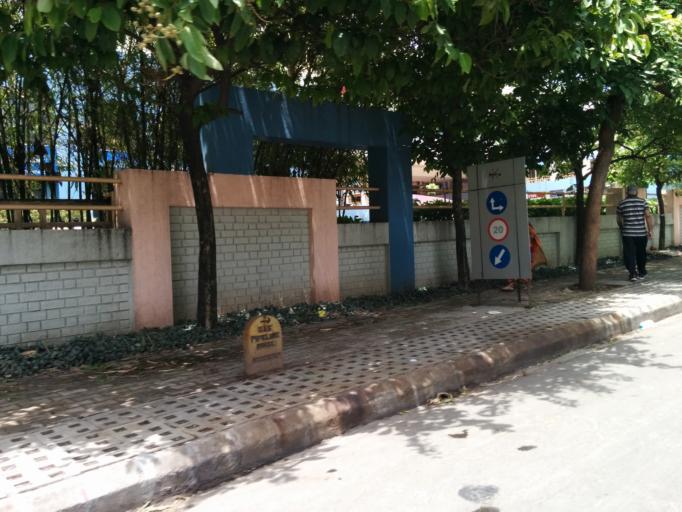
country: IN
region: Maharashtra
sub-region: Pune Division
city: Pune
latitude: 18.5103
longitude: 73.9288
